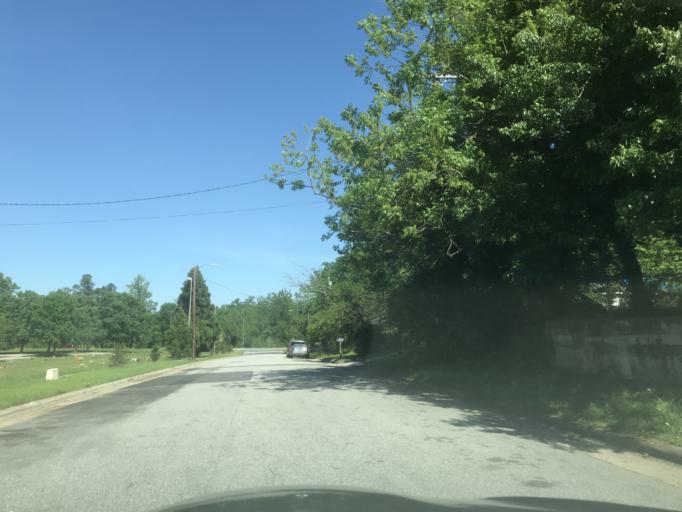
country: US
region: North Carolina
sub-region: Wake County
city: Raleigh
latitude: 35.7629
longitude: -78.6456
